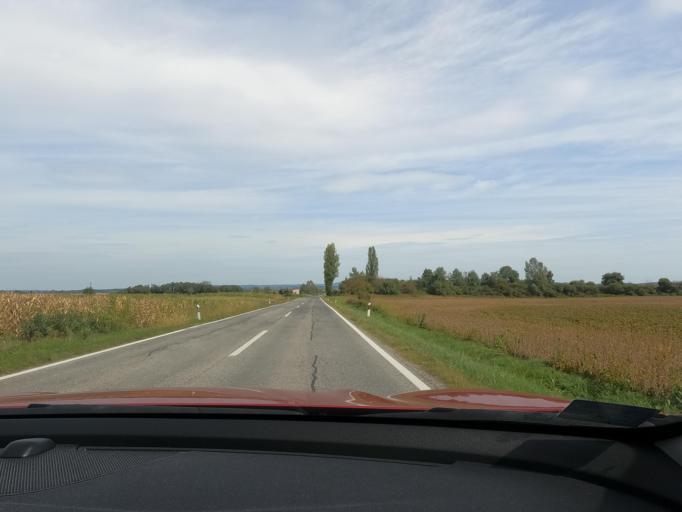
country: HR
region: Sisacko-Moslavacka
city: Osekovo
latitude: 45.5373
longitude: 16.5688
